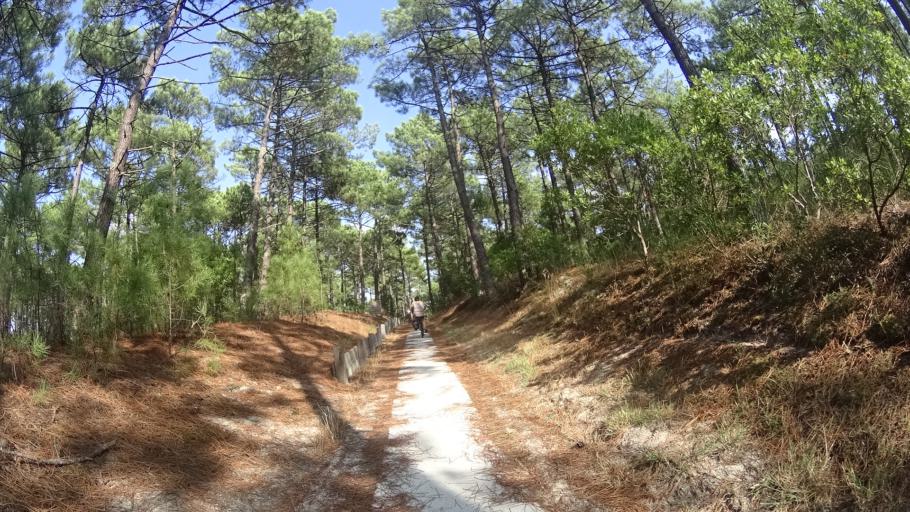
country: FR
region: Aquitaine
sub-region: Departement de la Gironde
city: Lacanau
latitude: 44.9635
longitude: -1.1963
